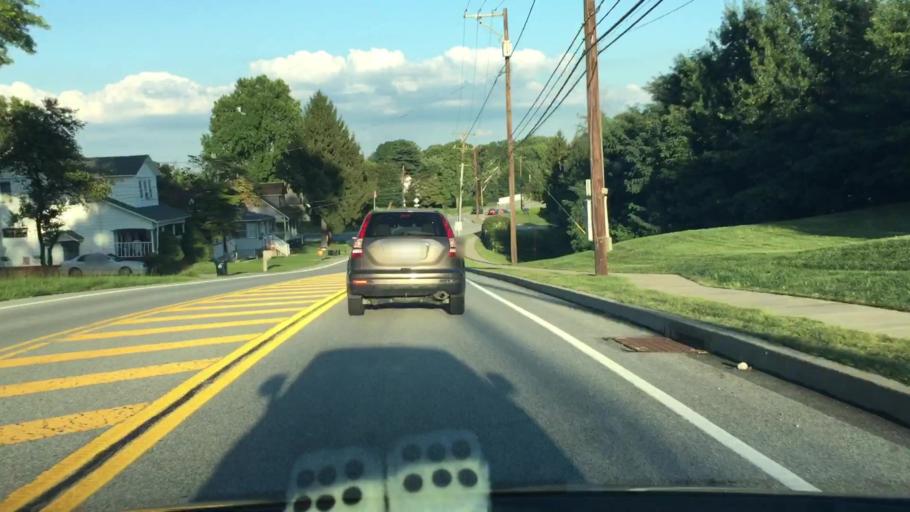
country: US
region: Pennsylvania
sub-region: Delaware County
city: Boothwyn
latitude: 39.8356
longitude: -75.4732
